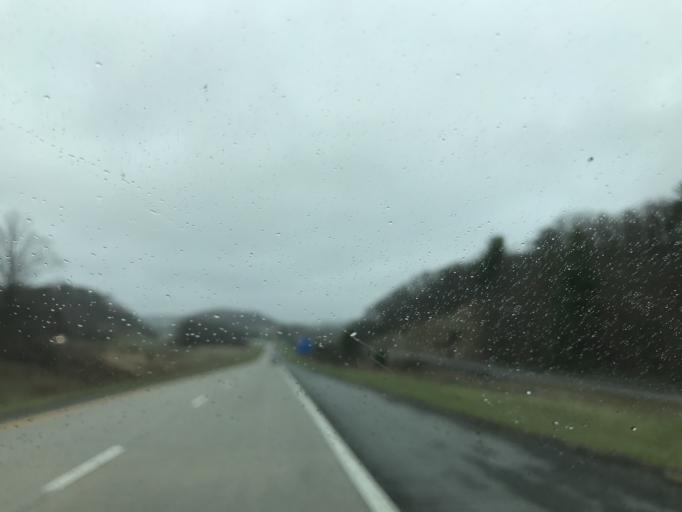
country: US
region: West Virginia
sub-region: Greenbrier County
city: Rainelle
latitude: 37.8413
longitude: -80.7423
